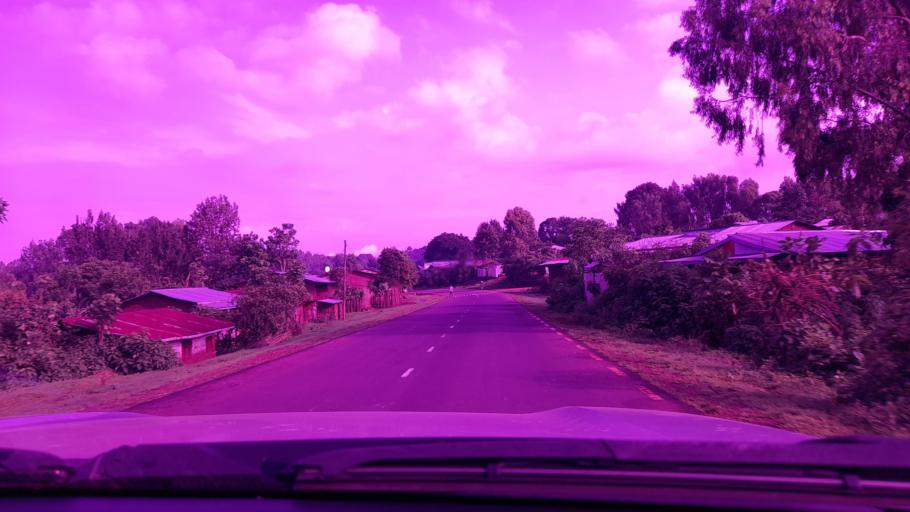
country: ET
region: Oromiya
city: Bedele
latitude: 8.1665
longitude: 36.4711
